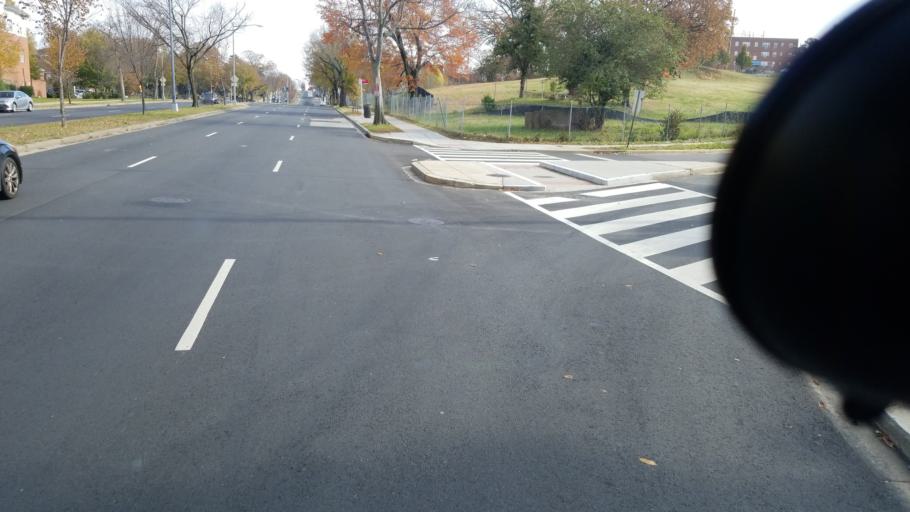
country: US
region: Maryland
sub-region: Prince George's County
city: Capitol Heights
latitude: 38.8897
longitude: -76.9345
